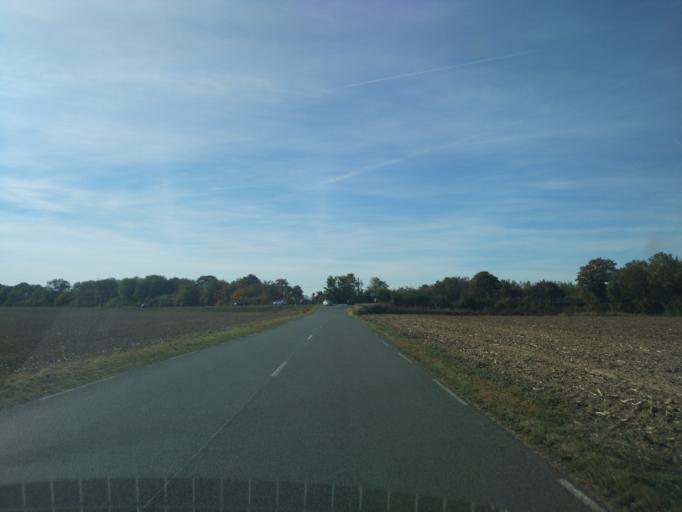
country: FR
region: Ile-de-France
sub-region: Departement de l'Essonne
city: Limours
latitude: 48.6543
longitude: 2.0793
